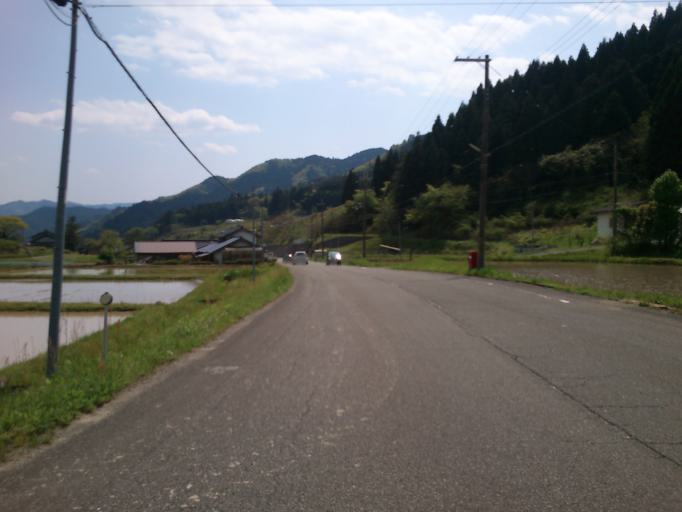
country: JP
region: Kyoto
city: Fukuchiyama
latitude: 35.3796
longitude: 134.9387
